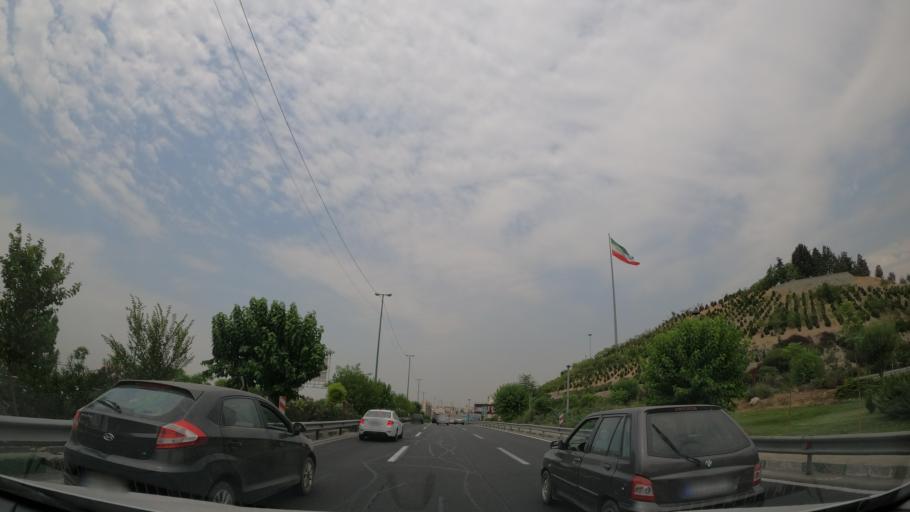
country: IR
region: Tehran
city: Tehran
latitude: 35.7408
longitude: 51.3449
